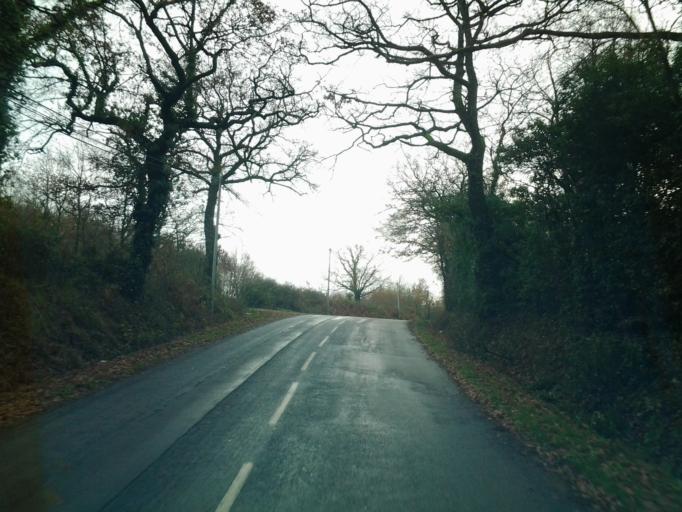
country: FR
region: Pays de la Loire
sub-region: Departement de la Vendee
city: La Roche-sur-Yon
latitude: 46.6576
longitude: -1.3950
